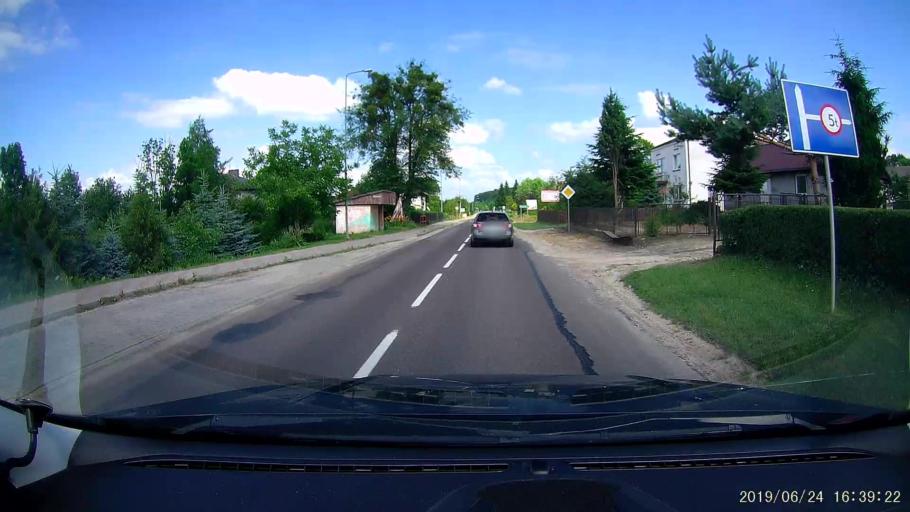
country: PL
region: Lublin Voivodeship
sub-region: Powiat tomaszowski
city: Rachanie
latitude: 50.5298
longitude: 23.5541
